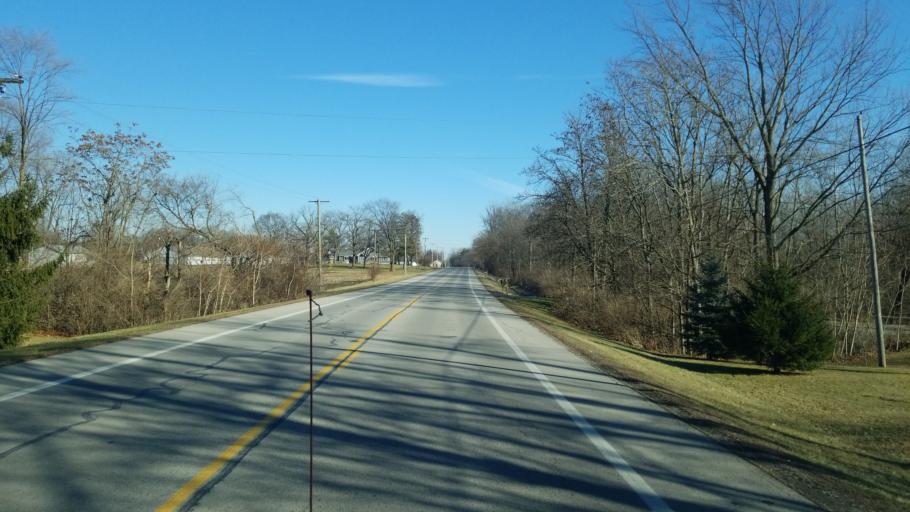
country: US
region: Ohio
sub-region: Wood County
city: Weston
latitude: 41.4298
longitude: -83.8419
